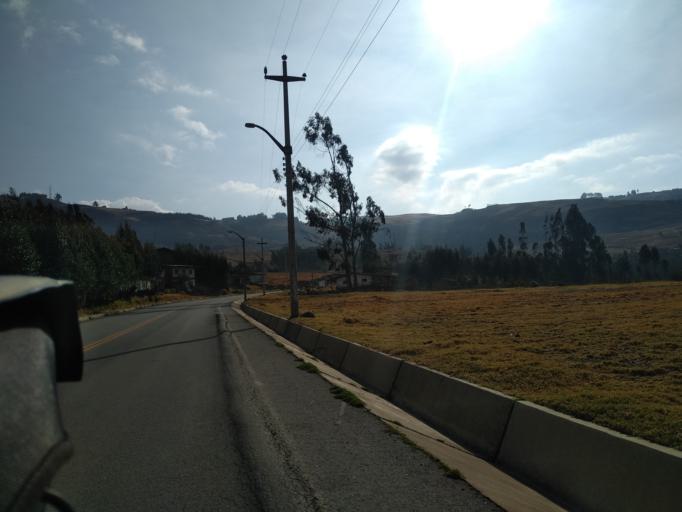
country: PE
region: La Libertad
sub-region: Provincia de Otuzco
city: Agallpampa
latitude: -7.9954
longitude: -78.5233
